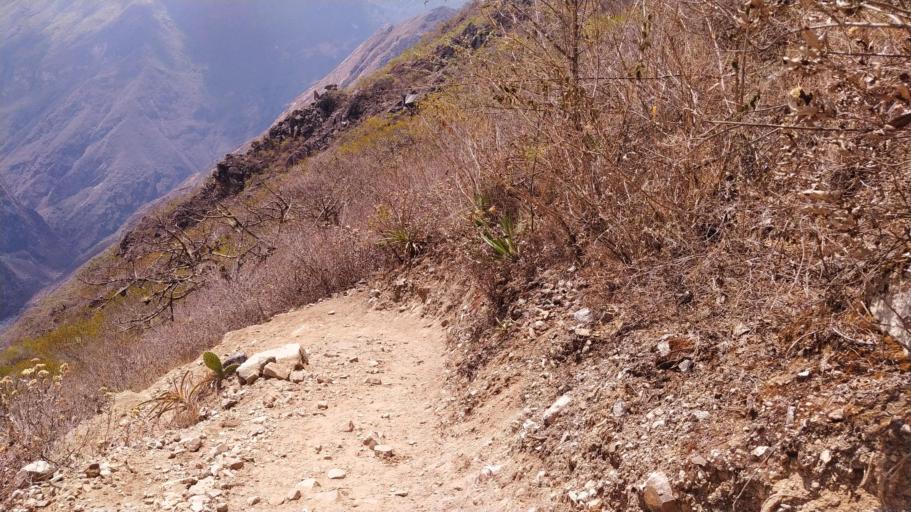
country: PE
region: Apurimac
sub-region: Provincia de Abancay
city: Cachora
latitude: -13.4334
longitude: -72.8244
